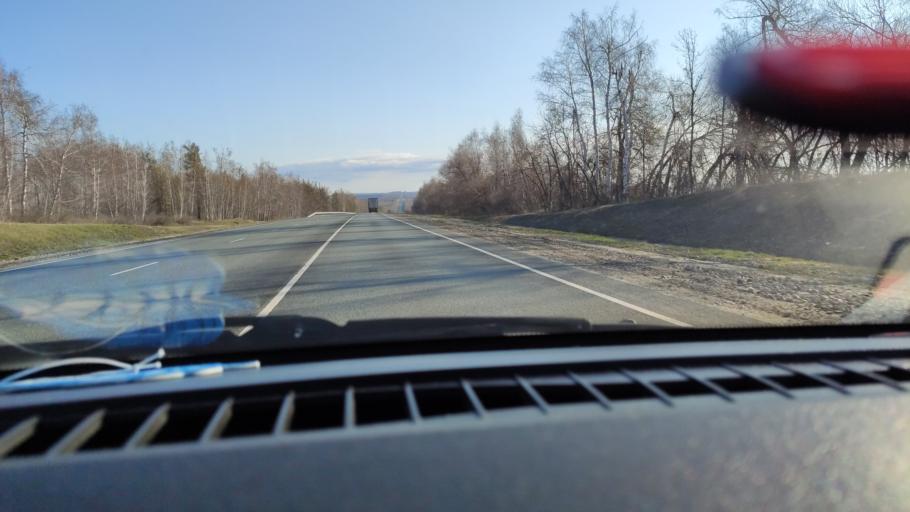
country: RU
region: Saratov
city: Khvalynsk
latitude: 52.5610
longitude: 48.0888
